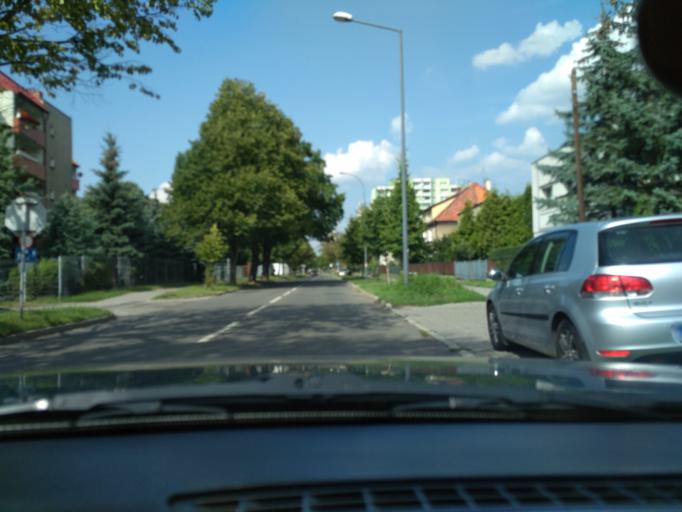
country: PL
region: Silesian Voivodeship
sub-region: Powiat raciborski
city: Raciborz
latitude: 50.0832
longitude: 18.2028
